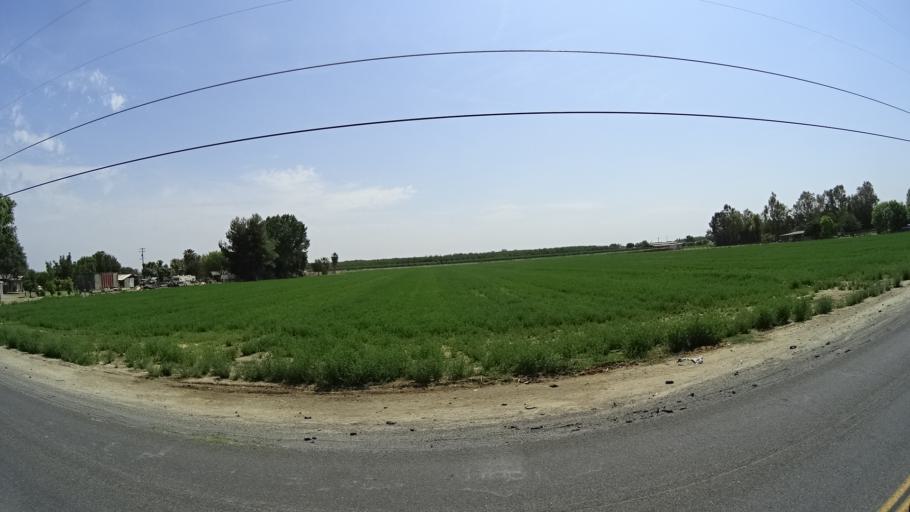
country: US
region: California
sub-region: Kings County
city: Lemoore
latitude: 36.3014
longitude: -119.7629
